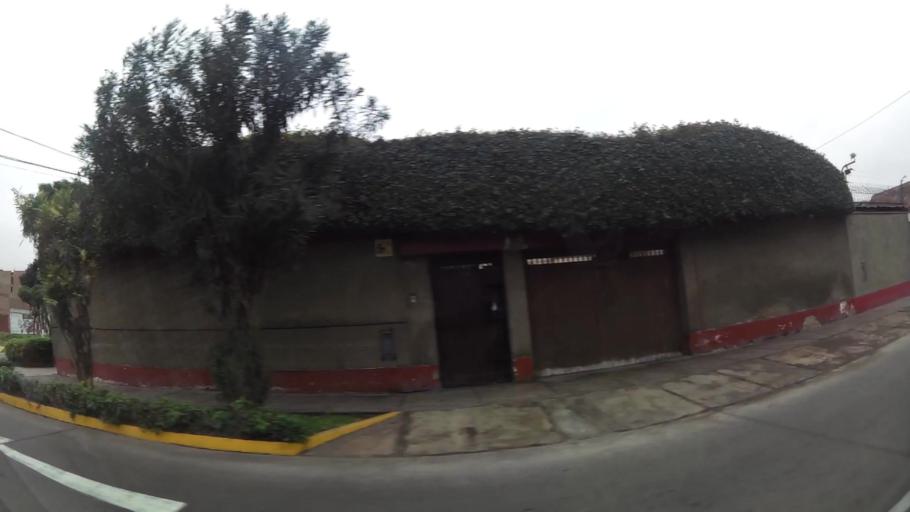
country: PE
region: Callao
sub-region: Callao
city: Callao
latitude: -12.0840
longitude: -77.0818
